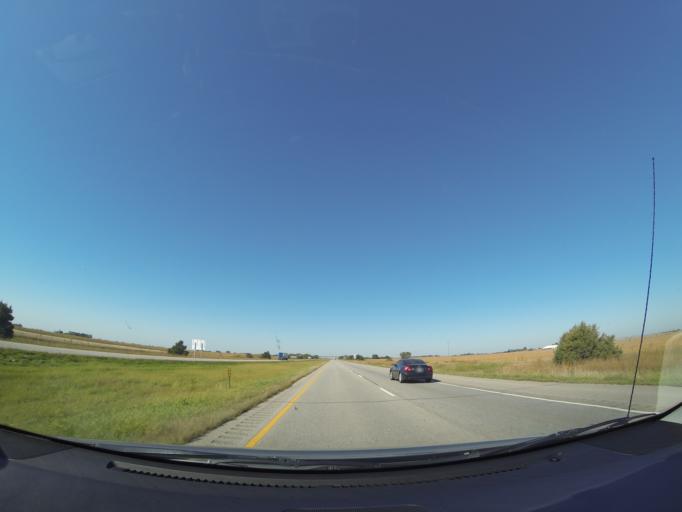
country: US
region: Nebraska
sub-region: Seward County
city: Milford
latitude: 40.8223
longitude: -97.1122
